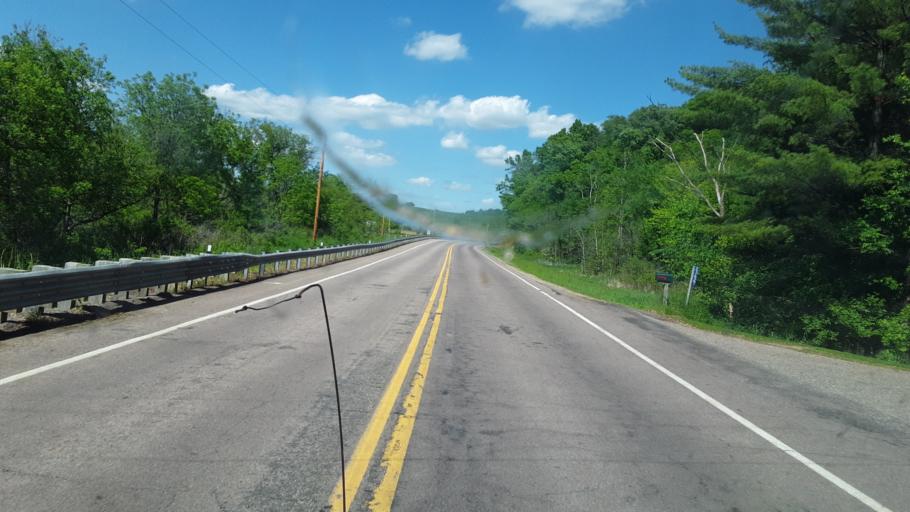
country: US
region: Wisconsin
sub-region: Richland County
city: Richland Center
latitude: 43.3568
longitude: -90.2698
